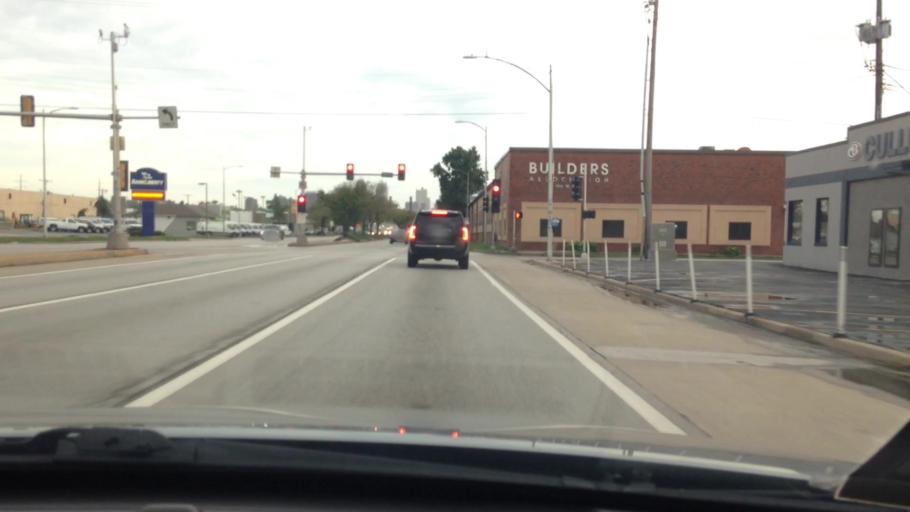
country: US
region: Missouri
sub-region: Clay County
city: North Kansas City
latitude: 39.1311
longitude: -94.5807
